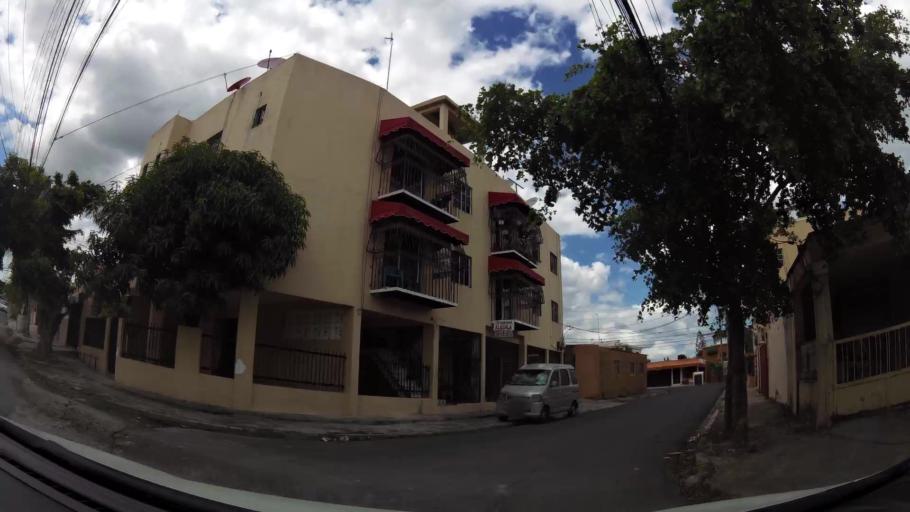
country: DO
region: Nacional
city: Ensanche Luperon
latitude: 18.5184
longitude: -69.9050
